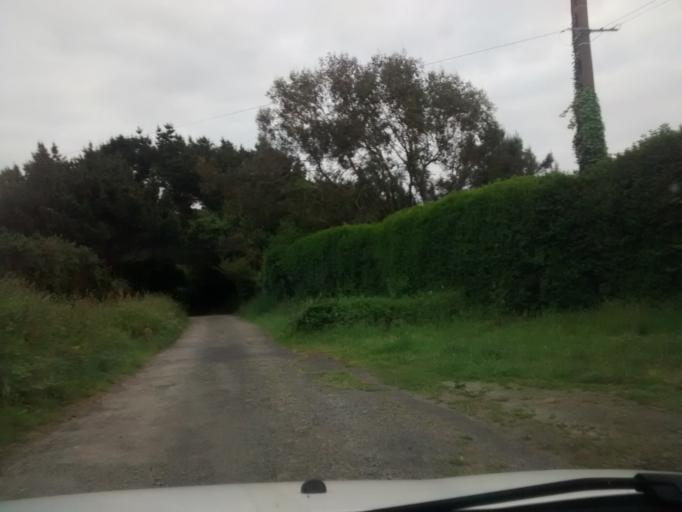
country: FR
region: Brittany
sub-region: Departement des Cotes-d'Armor
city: Tregastel
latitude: 48.8273
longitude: -3.4794
